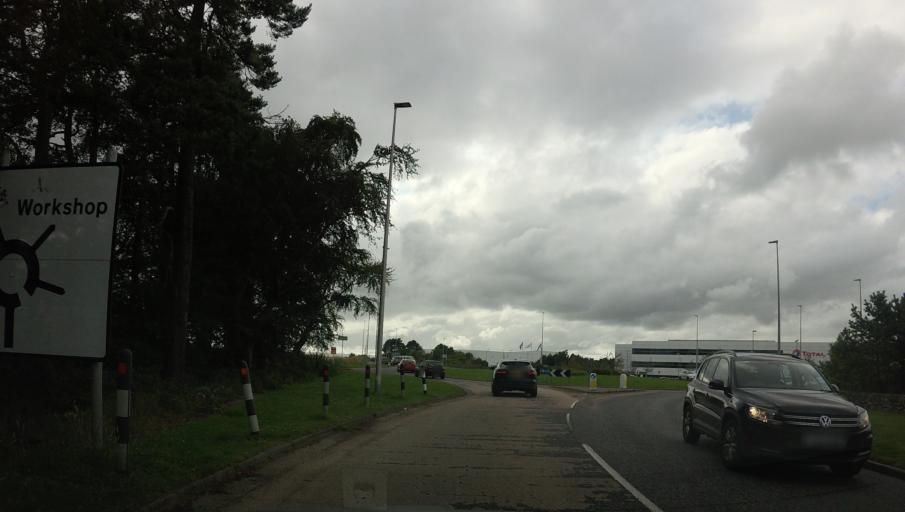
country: GB
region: Scotland
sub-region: Aberdeenshire
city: Westhill
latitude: 57.1441
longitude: -2.2897
